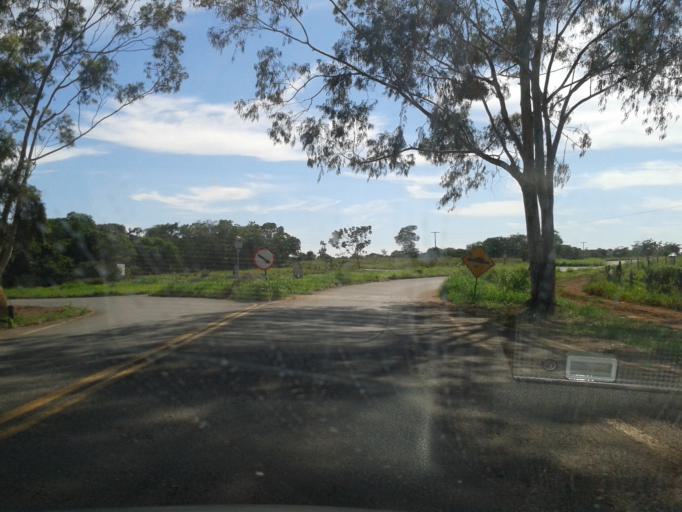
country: BR
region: Goias
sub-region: Piracanjuba
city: Piracanjuba
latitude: -17.2312
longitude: -48.7123
